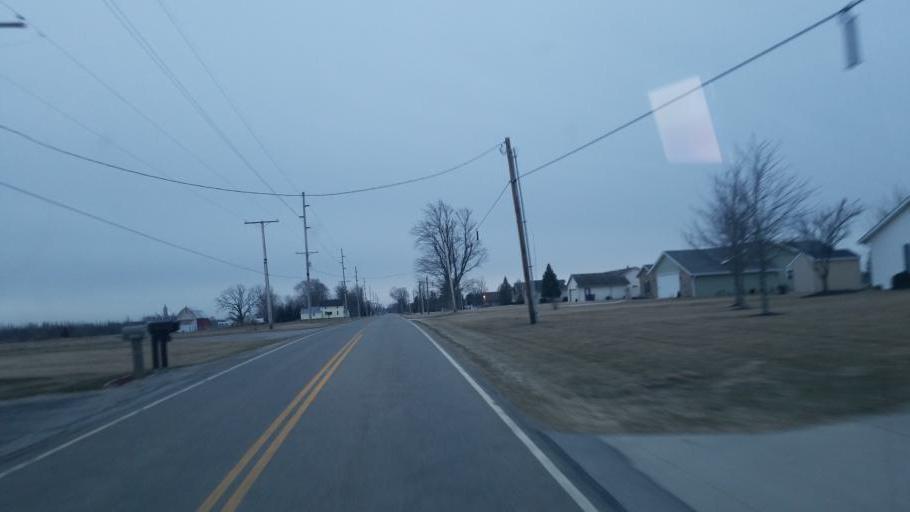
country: US
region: Ohio
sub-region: Defiance County
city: Hicksville
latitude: 41.3152
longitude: -84.7667
